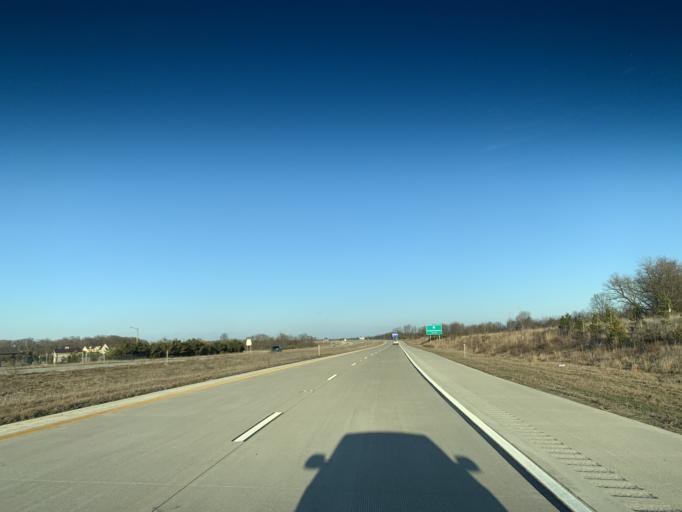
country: US
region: Delaware
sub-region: New Castle County
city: Middletown
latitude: 39.4743
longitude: -75.7312
